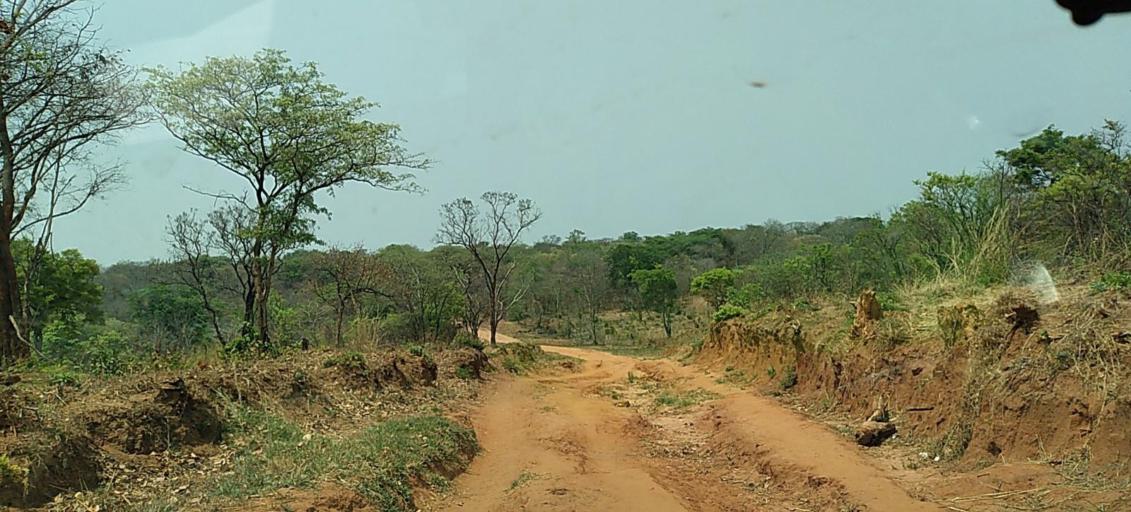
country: ZM
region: Western
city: Lukulu
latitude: -13.9820
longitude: 23.2281
